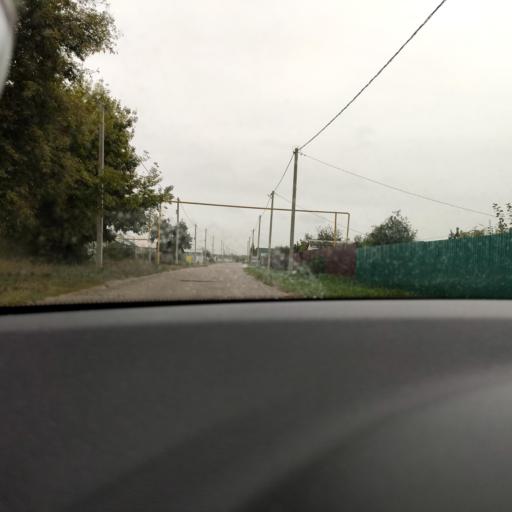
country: RU
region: Samara
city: Yelkhovka
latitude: 53.7358
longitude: 50.3166
